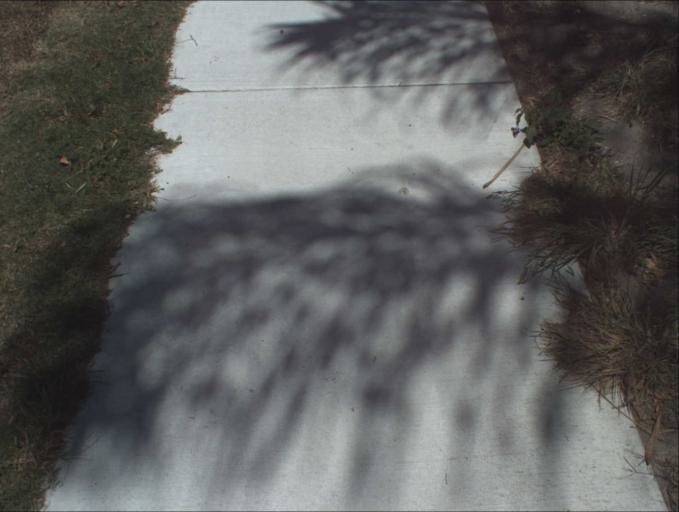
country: AU
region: Queensland
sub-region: Logan
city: Beenleigh
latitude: -27.7049
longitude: 153.2074
